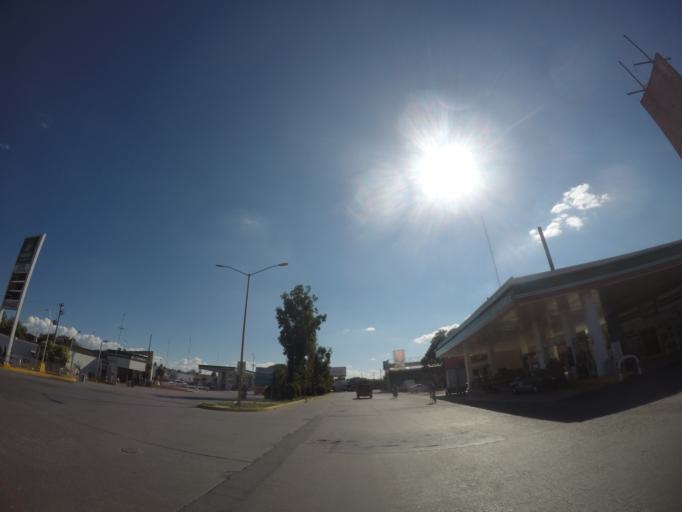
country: MX
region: San Luis Potosi
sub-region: San Luis Potosi
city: San Luis Potosi
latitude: 22.1701
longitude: -100.9714
